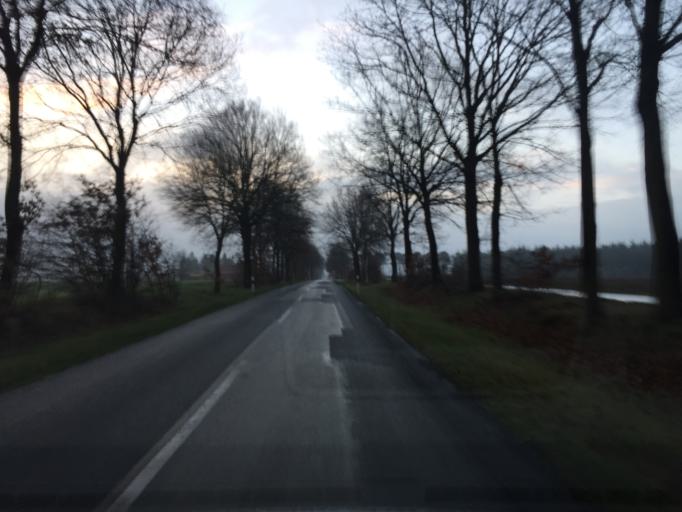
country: DE
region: Lower Saxony
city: Pennigsehl
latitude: 52.6273
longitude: 9.0435
